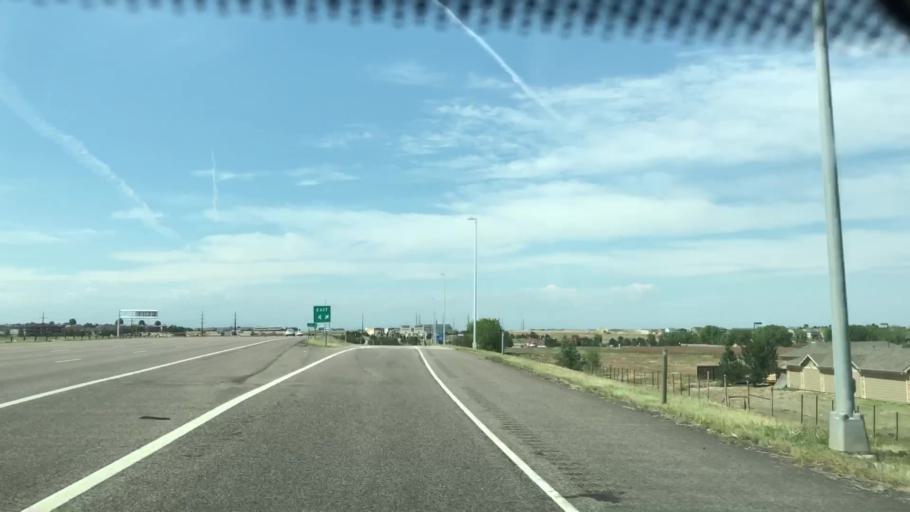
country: US
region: Colorado
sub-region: Douglas County
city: Stonegate
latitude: 39.5487
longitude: -104.7881
